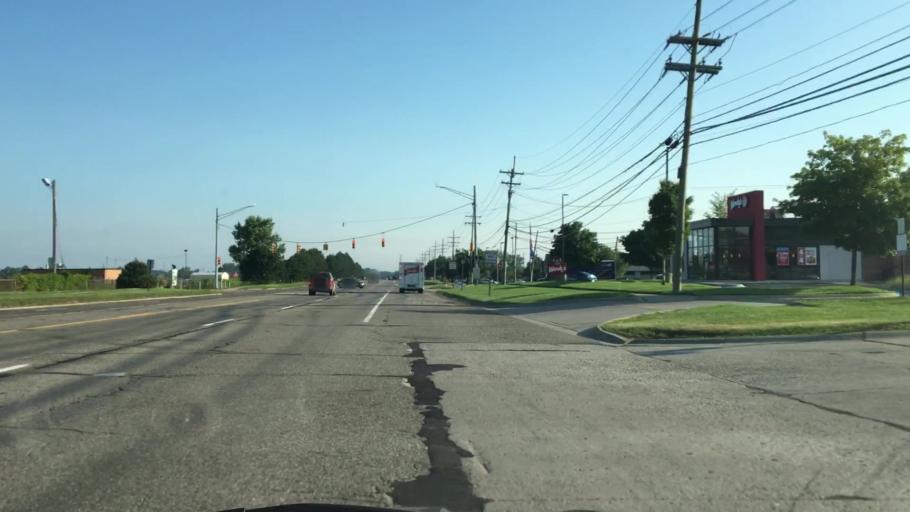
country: US
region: Michigan
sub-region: Oakland County
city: Wixom
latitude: 42.5071
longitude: -83.5365
